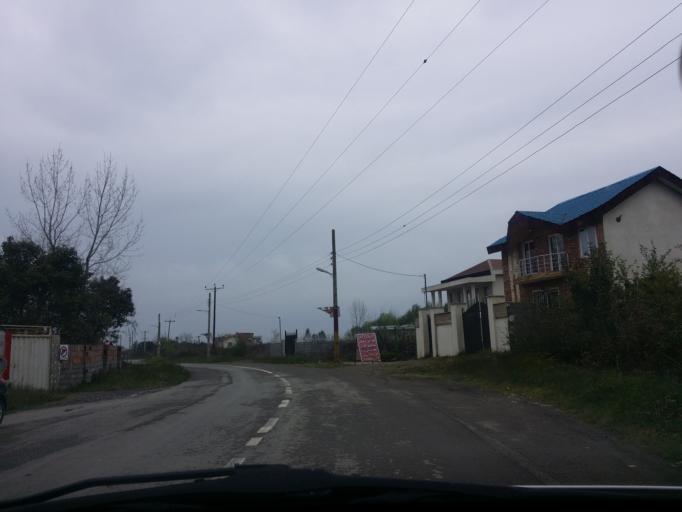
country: IR
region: Mazandaran
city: Chalus
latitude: 36.6828
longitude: 51.3797
